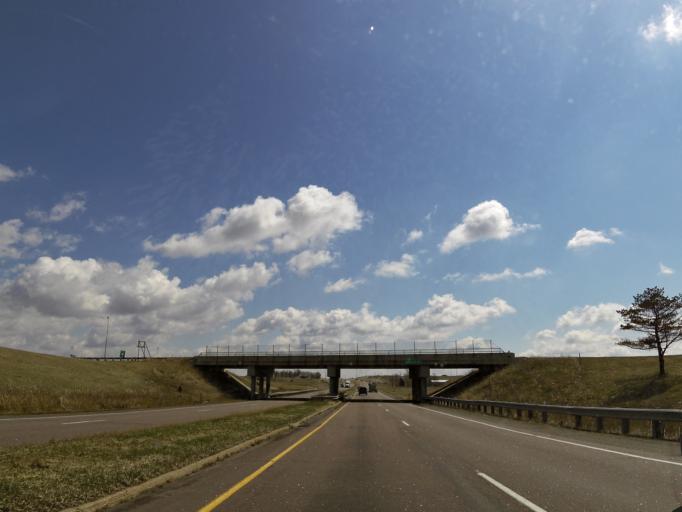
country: US
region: Minnesota
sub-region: Goodhue County
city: Cannon Falls
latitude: 44.6020
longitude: -92.9939
